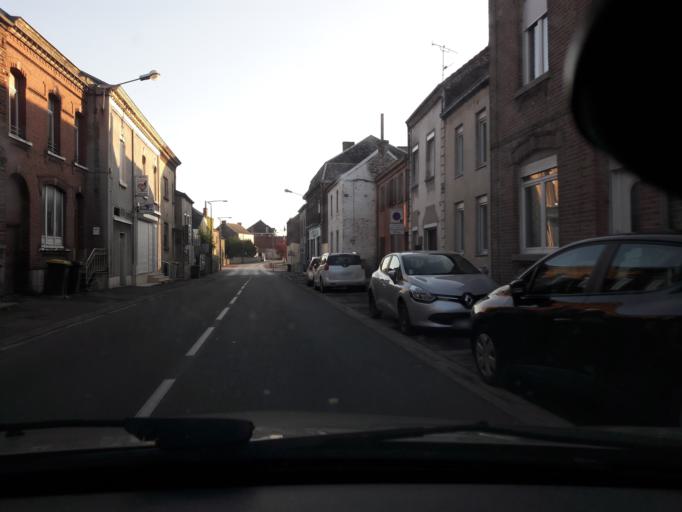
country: FR
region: Nord-Pas-de-Calais
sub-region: Departement du Nord
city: Marpent
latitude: 50.2924
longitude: 4.0819
